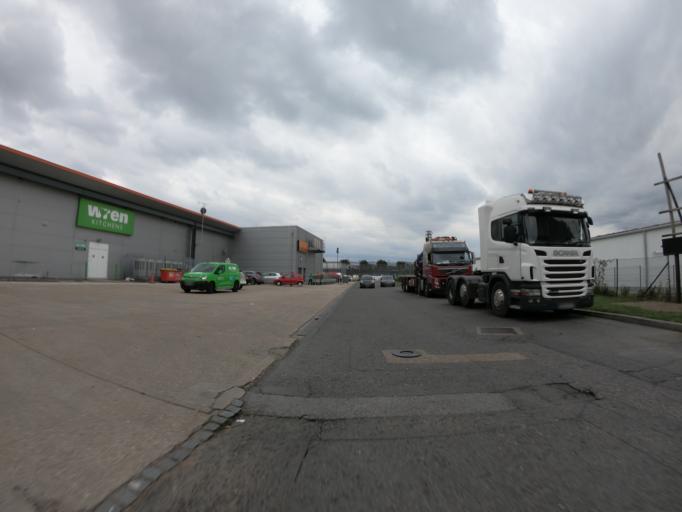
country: GB
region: England
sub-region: Greater London
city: Barking
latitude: 51.5211
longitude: 0.0701
